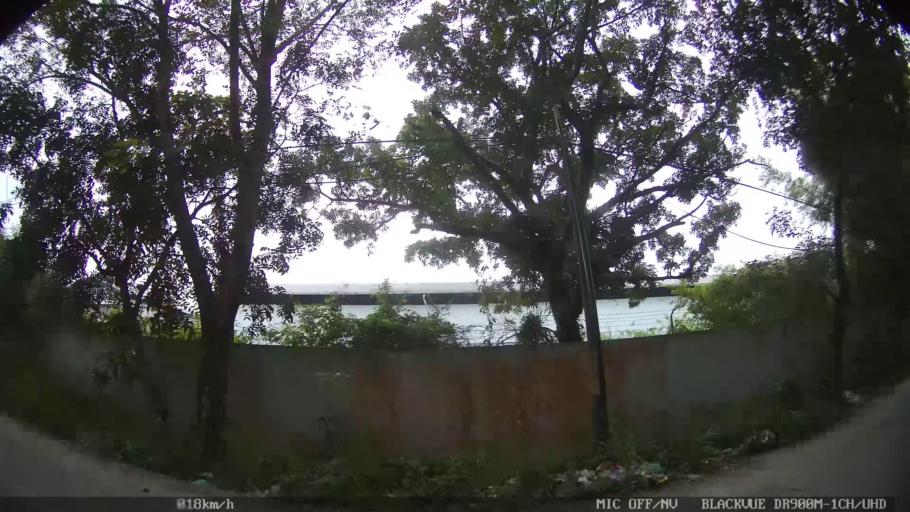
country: ID
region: North Sumatra
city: Deli Tua
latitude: 3.5381
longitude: 98.7264
